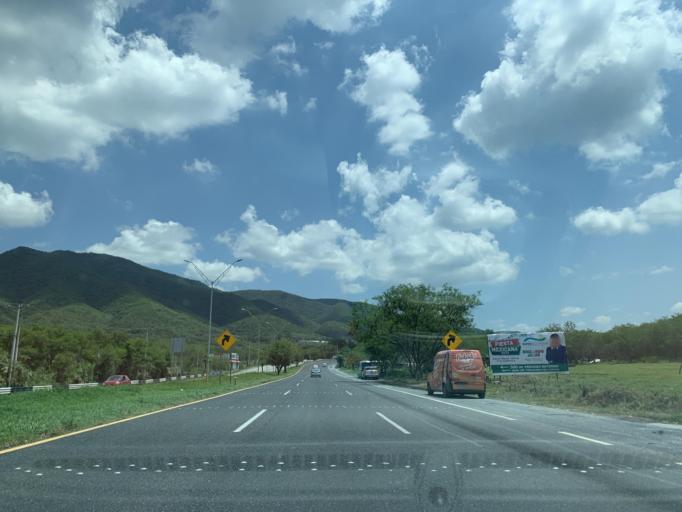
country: MX
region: Nuevo Leon
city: Santiago
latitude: 25.3971
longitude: -100.1258
